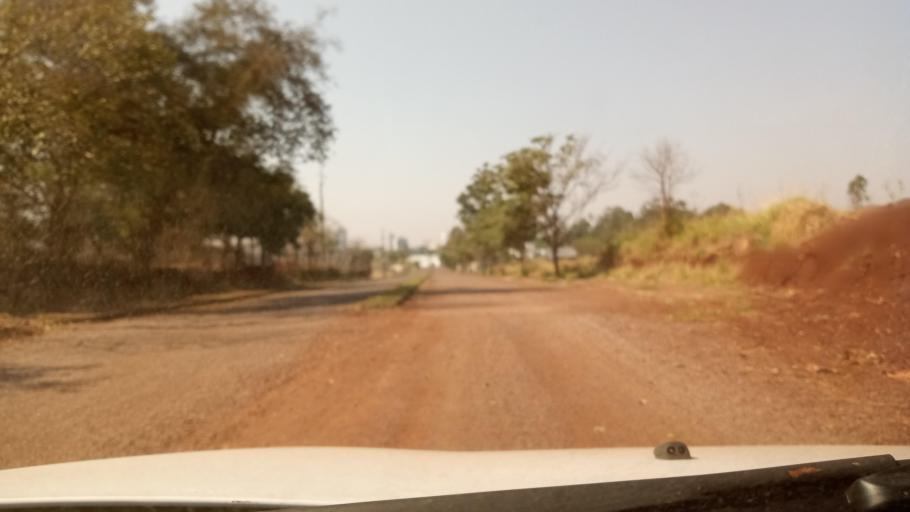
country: BR
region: Parana
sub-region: Toledo
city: Toledo
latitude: -24.7107
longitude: -53.7588
